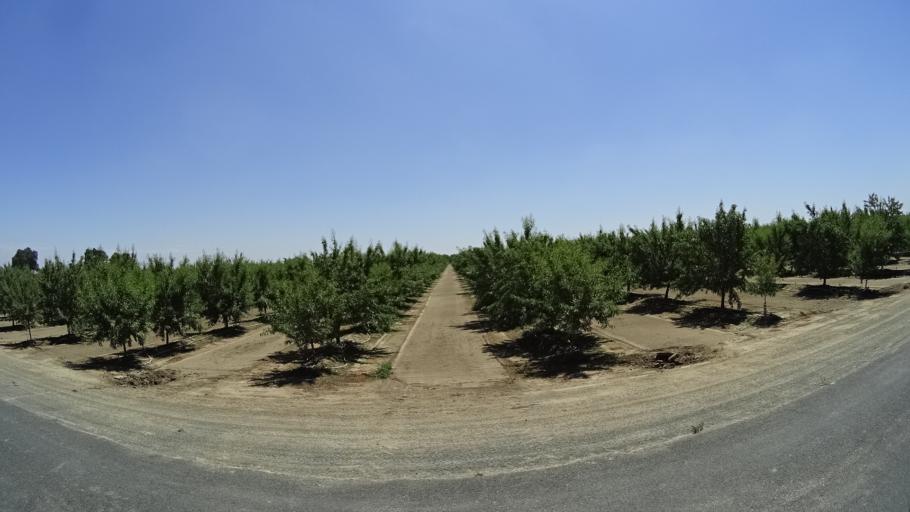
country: US
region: California
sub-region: Fresno County
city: Laton
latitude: 36.4158
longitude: -119.6572
